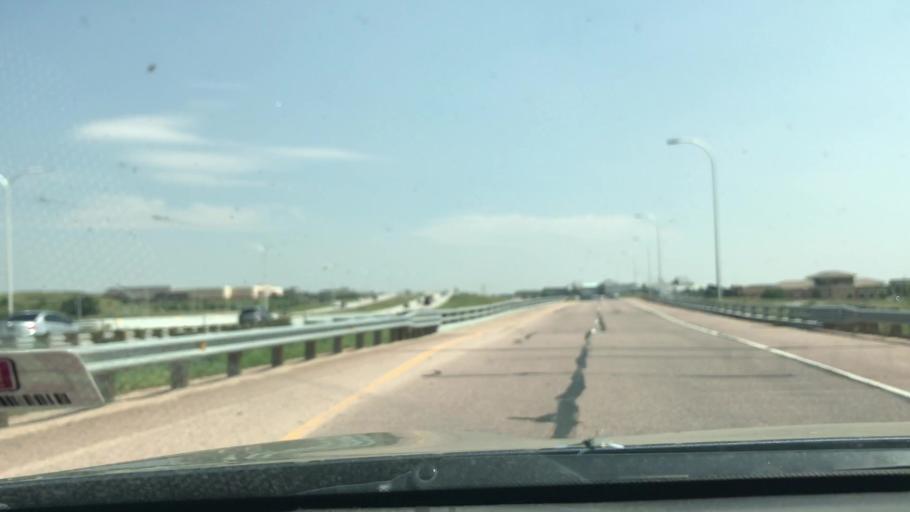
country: US
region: Colorado
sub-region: El Paso County
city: Black Forest
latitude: 38.9761
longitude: -104.7537
